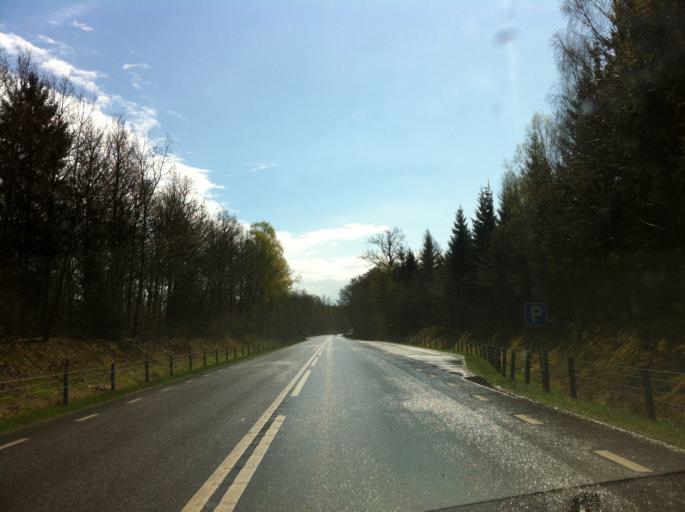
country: SE
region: Skane
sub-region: Horby Kommun
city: Hoerby
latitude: 55.9000
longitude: 13.6151
